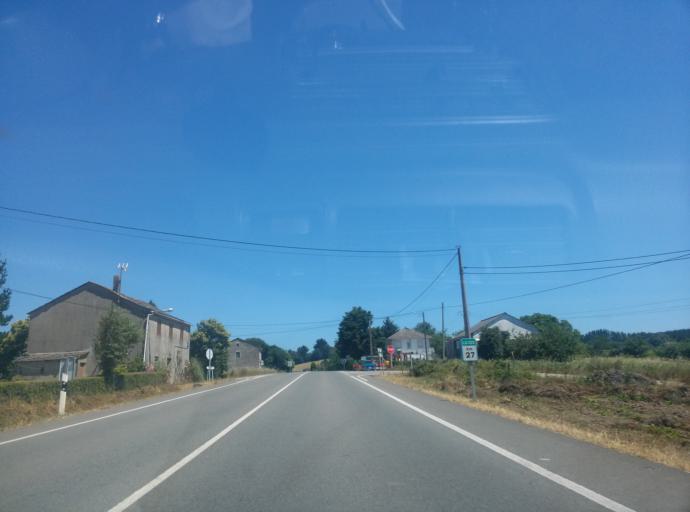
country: ES
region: Galicia
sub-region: Provincia de Lugo
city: Castro de Rei
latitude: 43.2314
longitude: -7.3502
